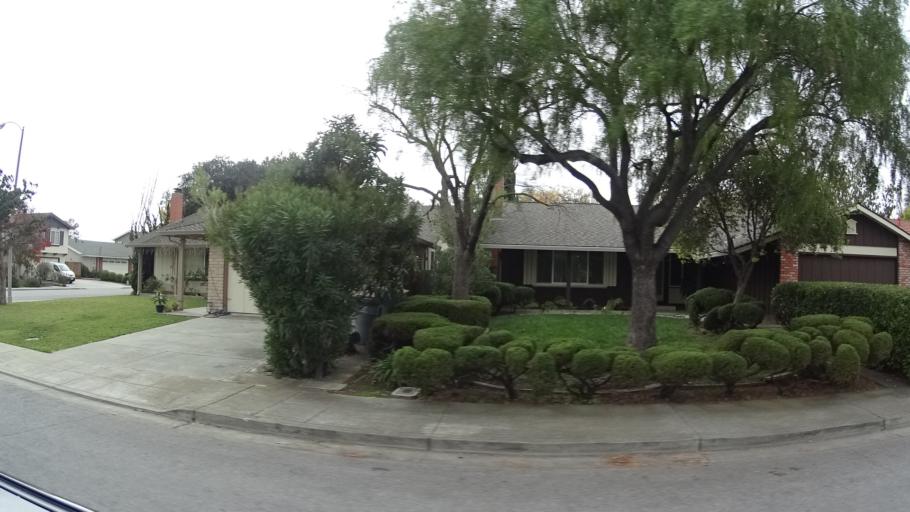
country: US
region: California
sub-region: Santa Clara County
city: Sunnyvale
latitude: 37.3647
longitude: -122.0009
